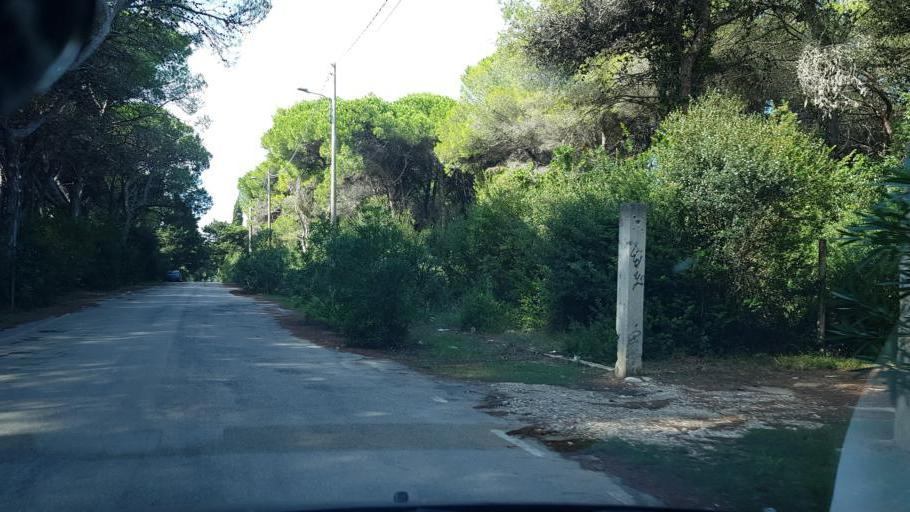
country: IT
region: Apulia
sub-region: Provincia di Lecce
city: Borgagne
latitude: 40.2323
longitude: 18.4570
